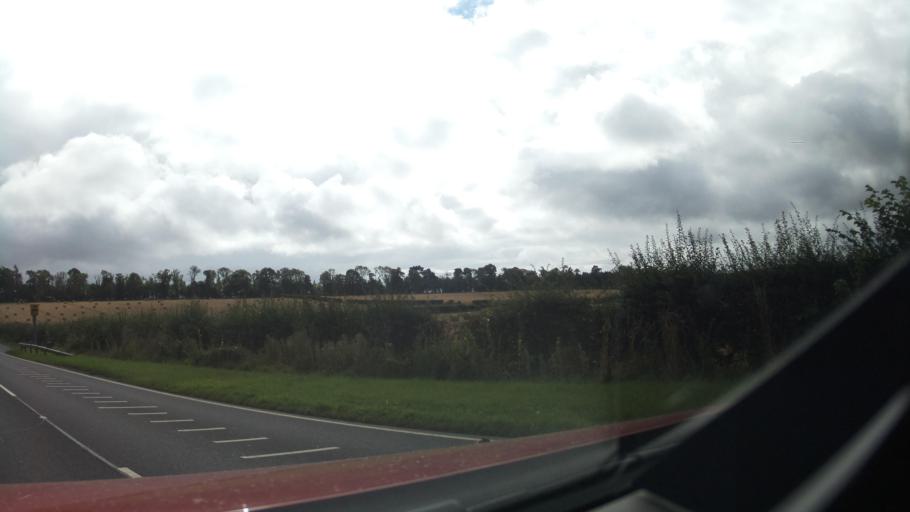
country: GB
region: Scotland
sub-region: The Scottish Borders
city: Saint Boswells
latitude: 55.5596
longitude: -2.6433
